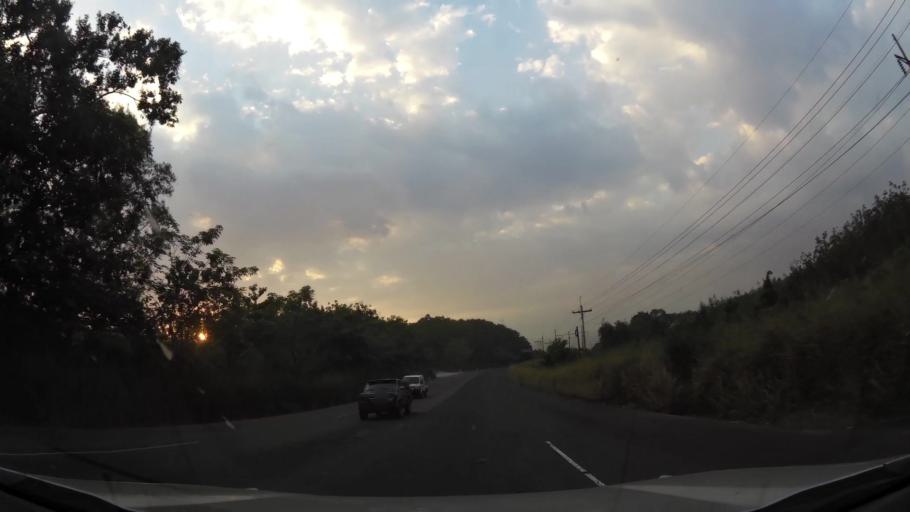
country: GT
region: Escuintla
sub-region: Municipio de La Democracia
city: La Democracia
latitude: 14.2717
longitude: -90.9048
